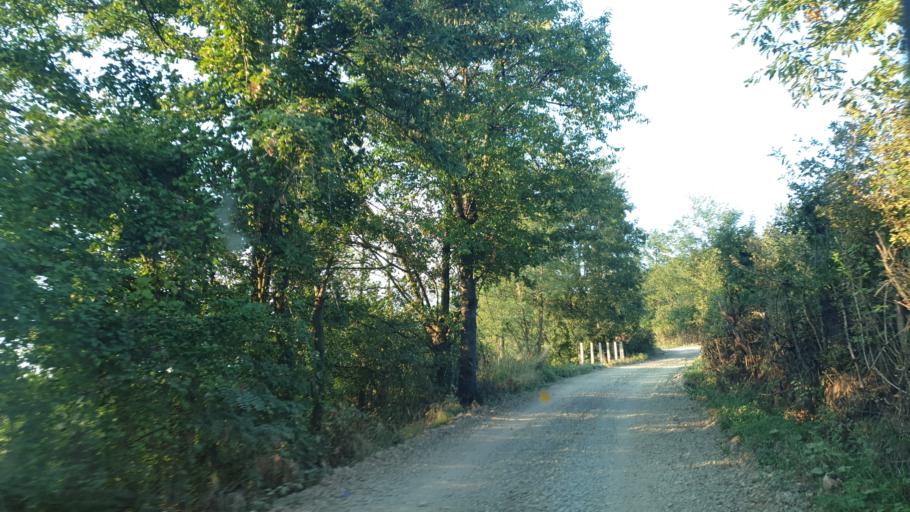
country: RS
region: Central Serbia
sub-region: Zlatiborski Okrug
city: Kosjeric
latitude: 43.9976
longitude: 20.0030
